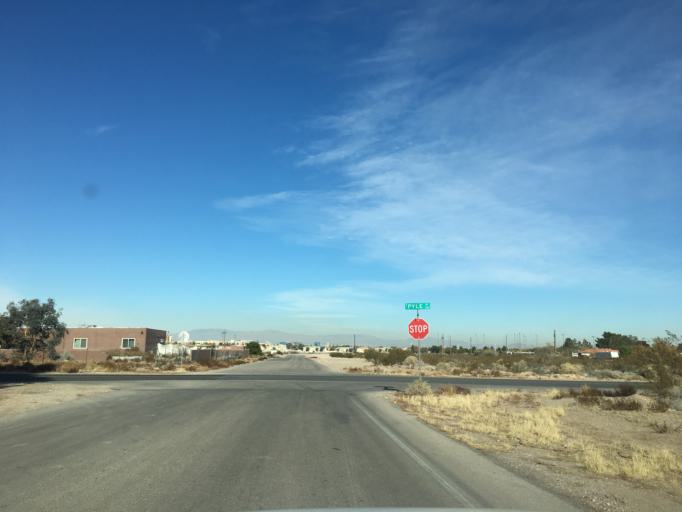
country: US
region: Nevada
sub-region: Clark County
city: Enterprise
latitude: 36.0062
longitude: -115.1680
